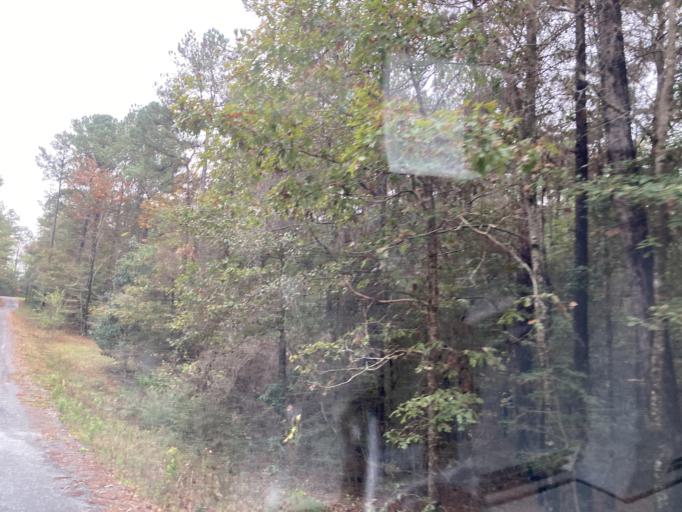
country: US
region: Mississippi
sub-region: Lamar County
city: Purvis
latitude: 31.1917
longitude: -89.4245
